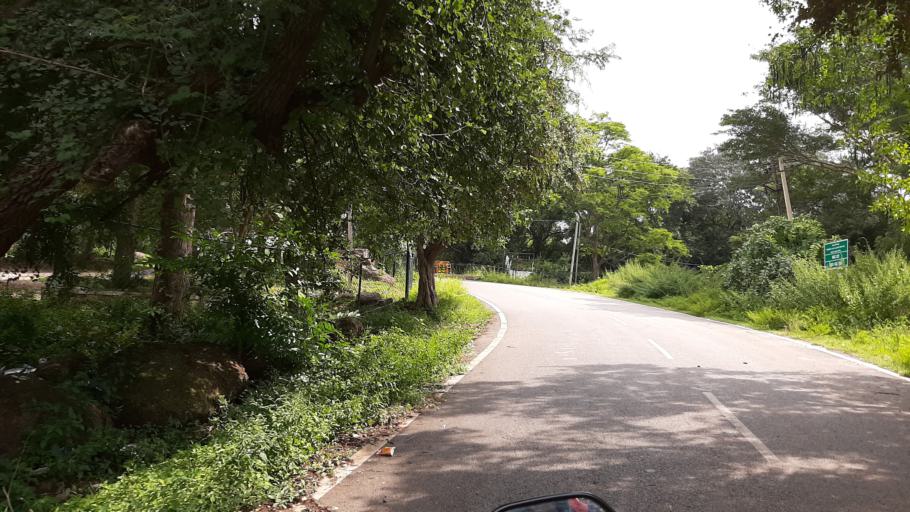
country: IN
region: Karnataka
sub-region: Ramanagara
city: Magadi
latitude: 12.9132
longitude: 77.2951
